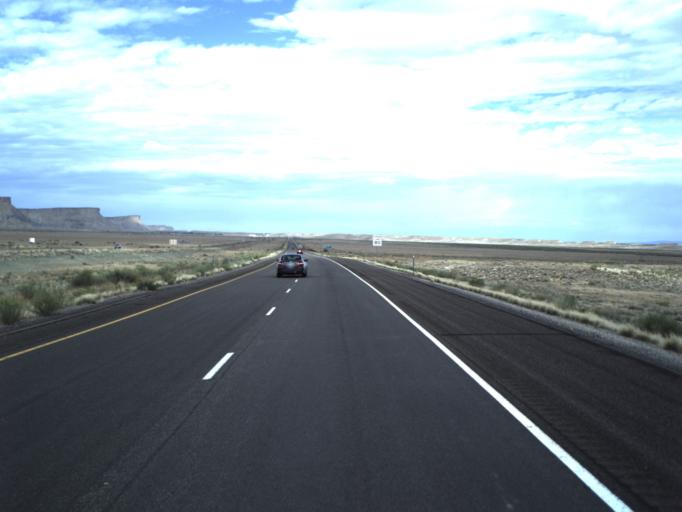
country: US
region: Utah
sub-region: Grand County
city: Moab
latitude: 38.9446
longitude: -109.7997
